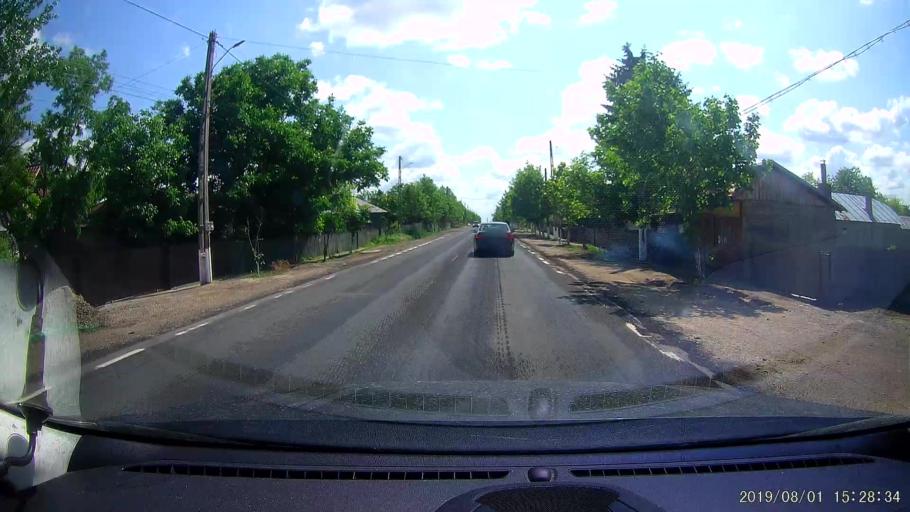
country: RO
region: Braila
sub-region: Comuna Viziru
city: Viziru
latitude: 44.9925
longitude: 27.7082
